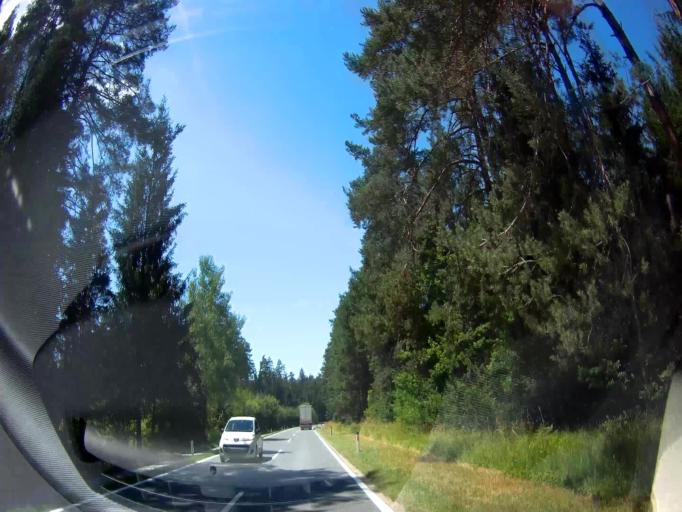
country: AT
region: Carinthia
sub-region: Politischer Bezirk Volkermarkt
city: Eberndorf
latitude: 46.6131
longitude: 14.6666
